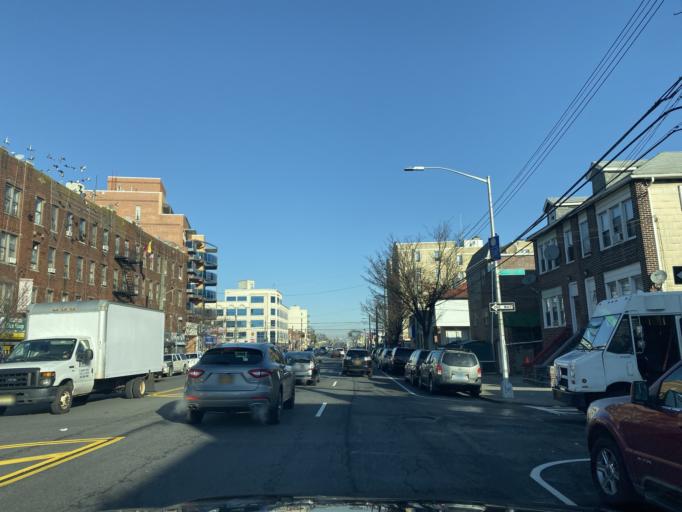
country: US
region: New York
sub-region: Kings County
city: Coney Island
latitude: 40.5808
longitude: -73.9598
